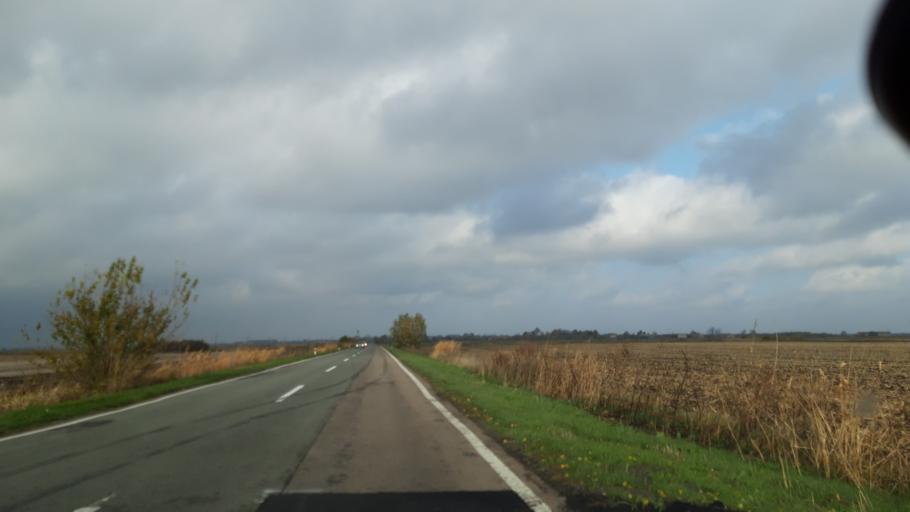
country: RS
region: Autonomna Pokrajina Vojvodina
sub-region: Severnobanatski Okrug
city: Coka
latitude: 45.9149
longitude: 20.1505
